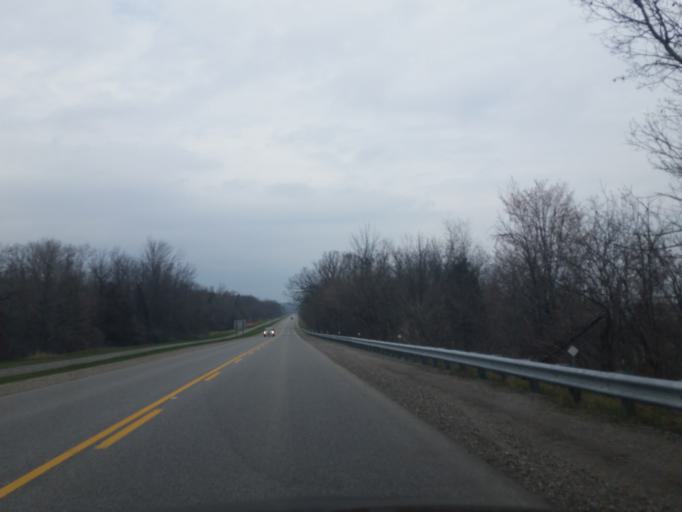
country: US
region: New York
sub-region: Jefferson County
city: Alexandria Bay
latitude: 44.3883
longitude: -75.9284
